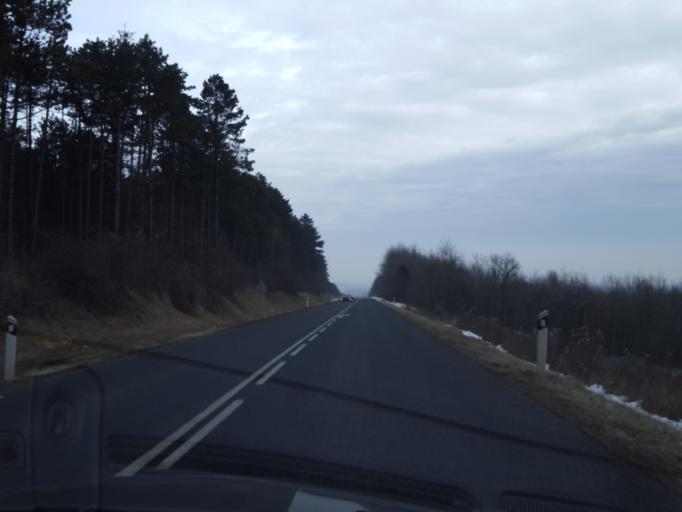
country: FR
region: Lorraine
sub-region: Departement de la Meuse
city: Verdun
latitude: 49.1805
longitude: 5.4851
